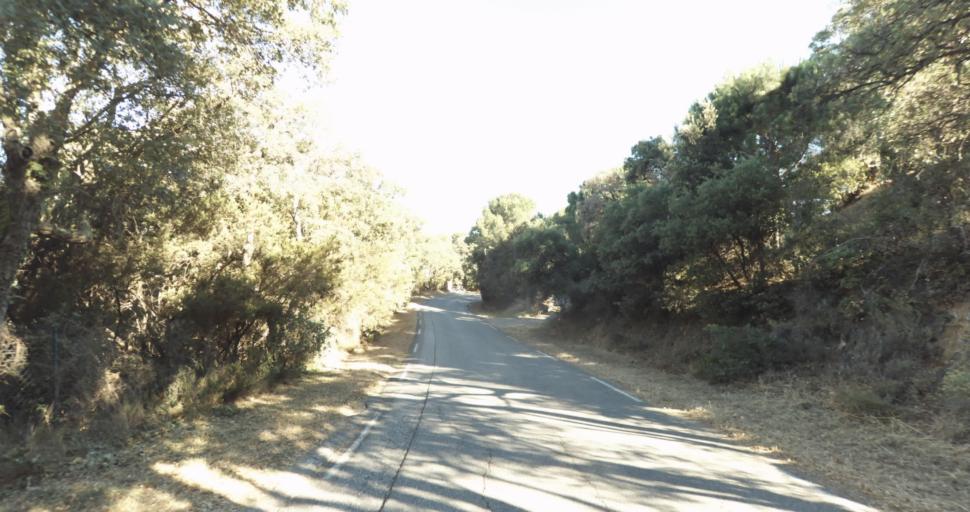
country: FR
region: Provence-Alpes-Cote d'Azur
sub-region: Departement du Var
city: Gassin
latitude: 43.2192
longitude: 6.5951
